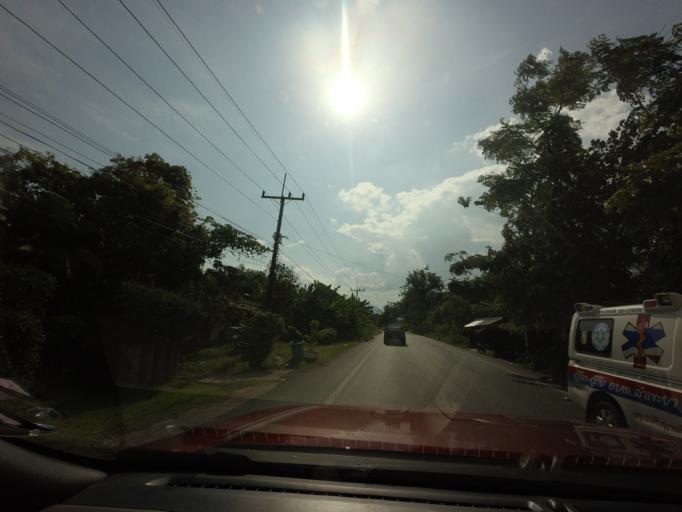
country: TH
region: Yala
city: Yala
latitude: 6.5569
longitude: 101.2230
